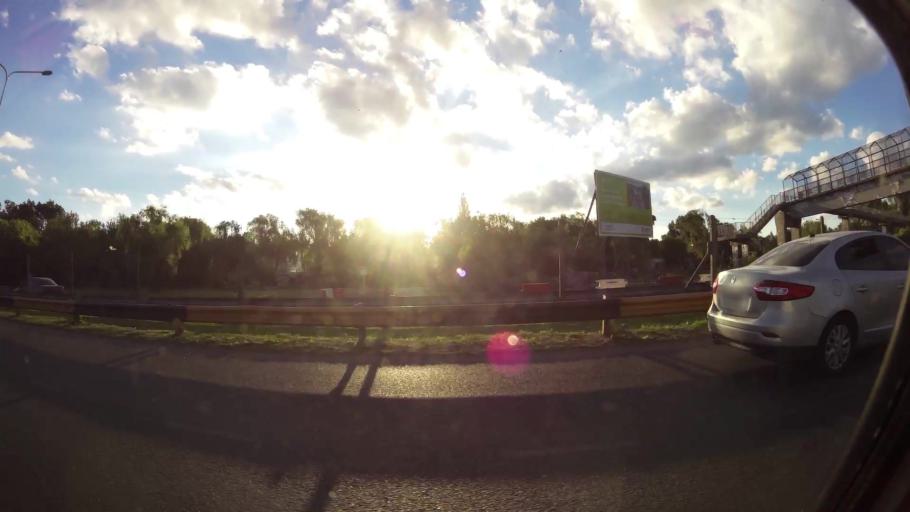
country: AR
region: Buenos Aires
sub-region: Partido de La Plata
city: La Plata
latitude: -34.8847
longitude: -57.9567
